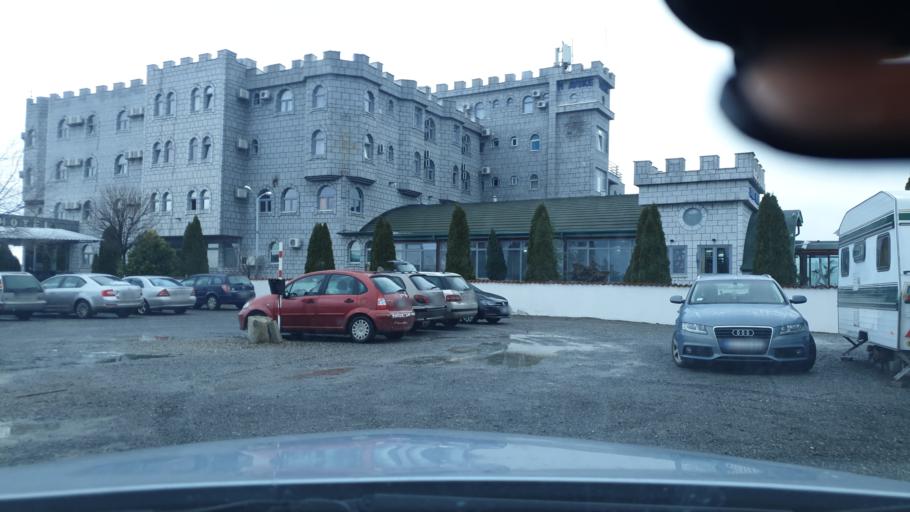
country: RS
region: Central Serbia
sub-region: Branicevski Okrug
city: Petrovac
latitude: 44.3065
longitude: 21.4841
